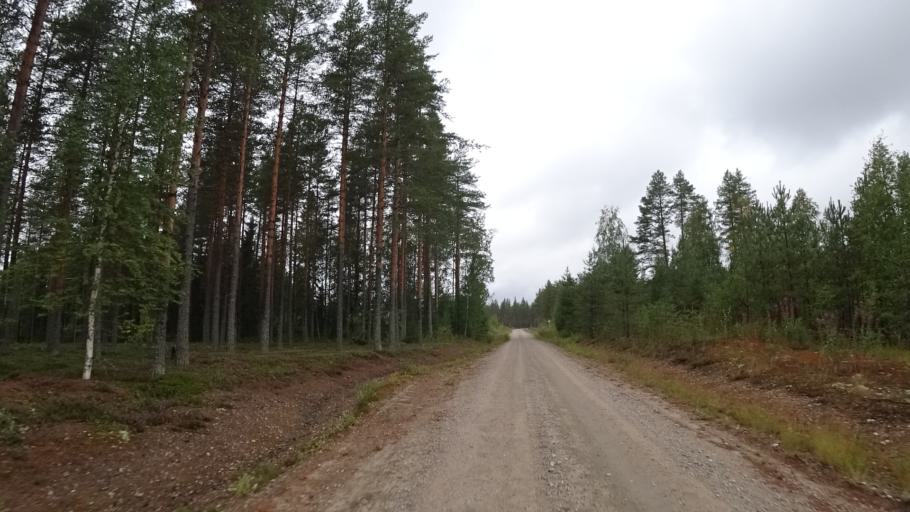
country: FI
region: North Karelia
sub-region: Pielisen Karjala
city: Lieksa
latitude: 63.5198
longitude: 30.1053
